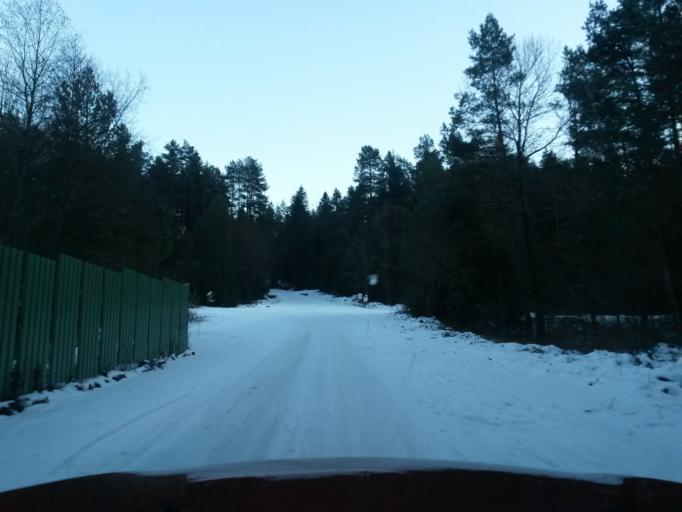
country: SK
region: Kosicky
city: Medzev
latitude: 48.7829
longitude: 20.7958
